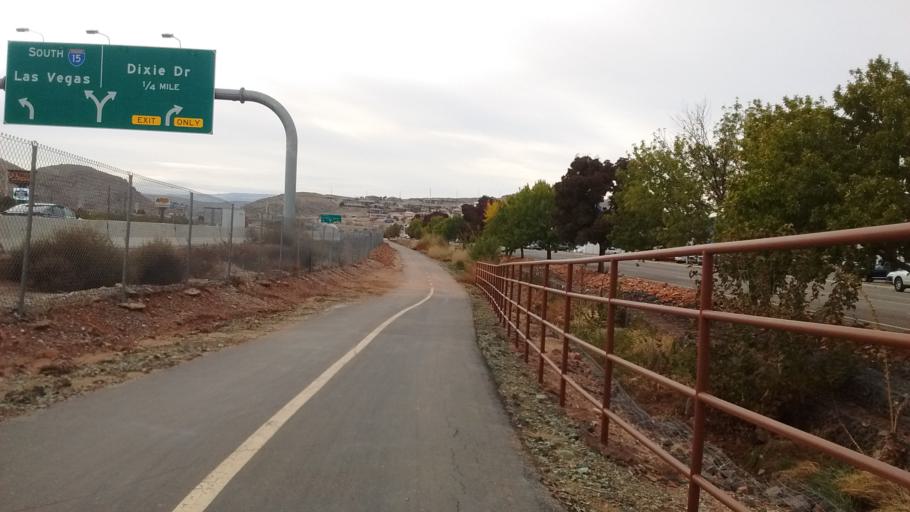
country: US
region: Utah
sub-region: Washington County
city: Saint George
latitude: 37.0817
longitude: -113.5844
